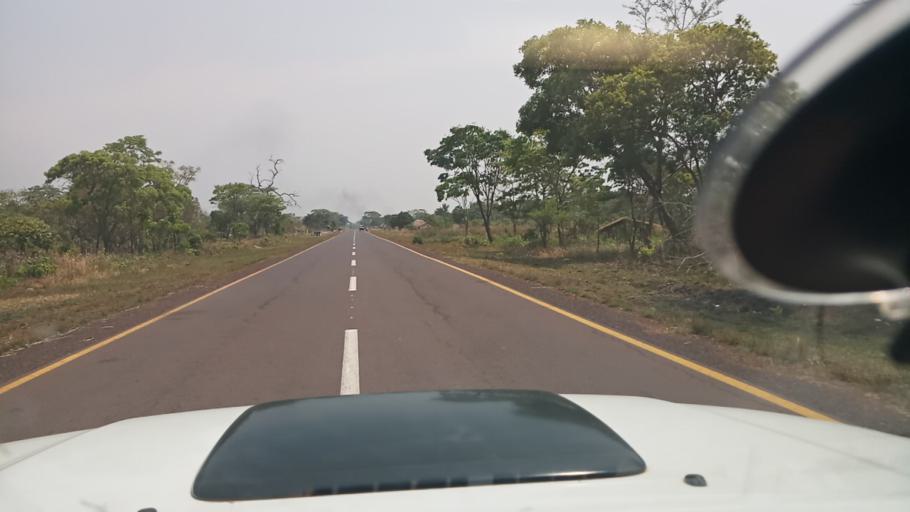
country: ZM
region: Luapula
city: Mwense
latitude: -10.8063
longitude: 28.2331
